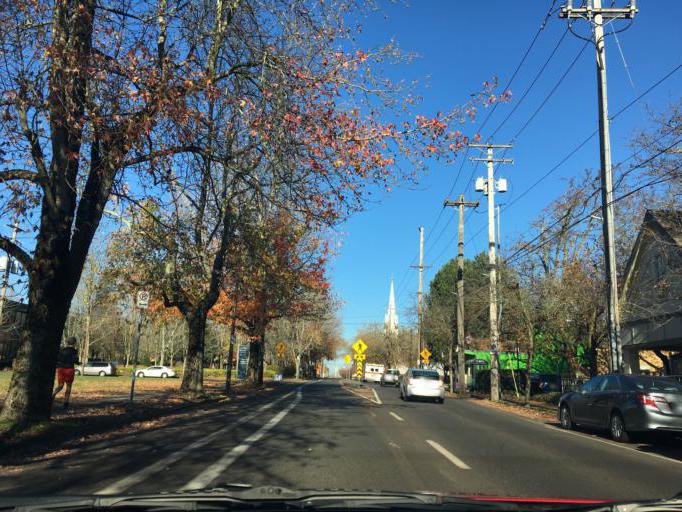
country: US
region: Oregon
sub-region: Multnomah County
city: Portland
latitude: 45.5422
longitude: -122.6667
